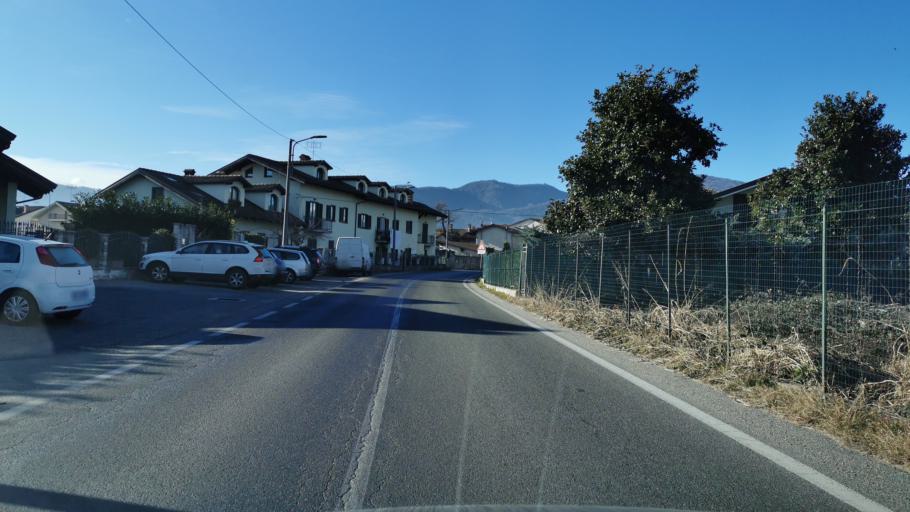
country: IT
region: Piedmont
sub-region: Provincia di Cuneo
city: Caraglio
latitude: 44.4191
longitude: 7.4353
